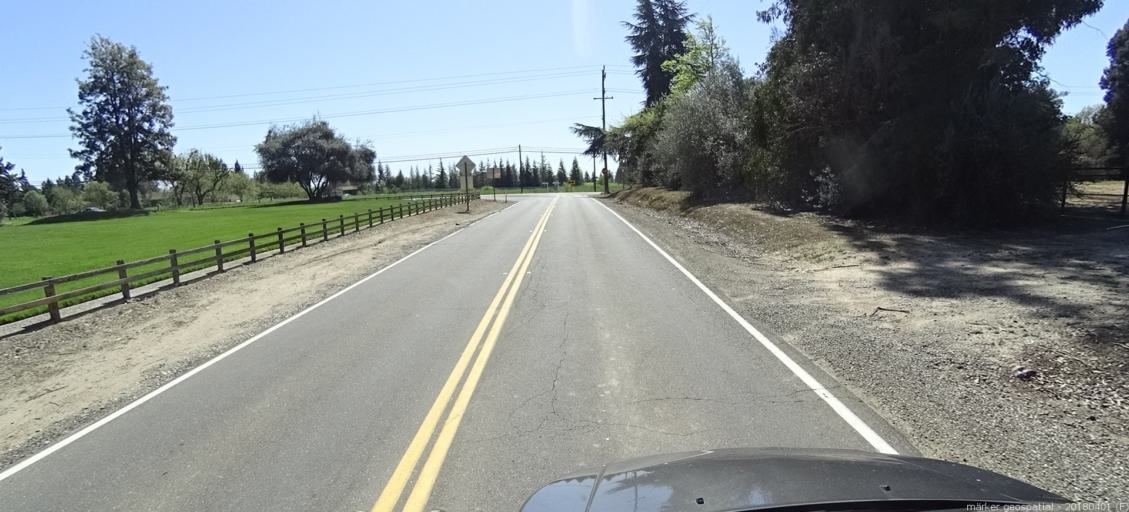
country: US
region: California
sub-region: Sacramento County
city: Wilton
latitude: 38.4168
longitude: -121.2303
